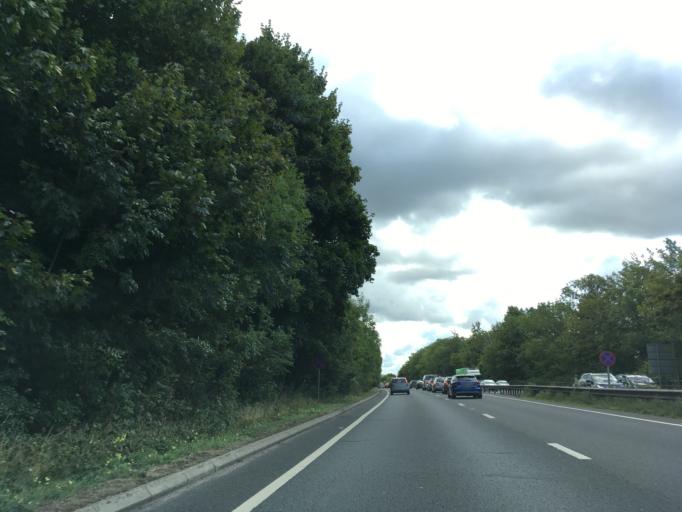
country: GB
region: England
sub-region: Hampshire
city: Winchester
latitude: 51.0992
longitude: -1.3360
